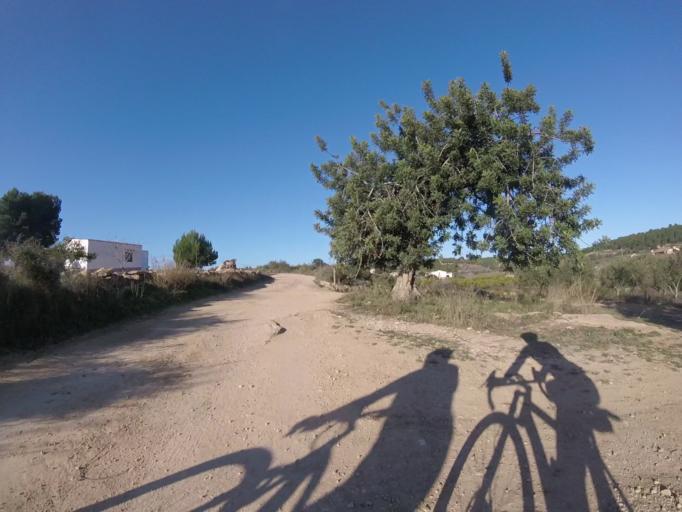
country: ES
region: Valencia
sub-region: Provincia de Castello
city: Torreblanca
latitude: 40.2508
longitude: 0.1851
